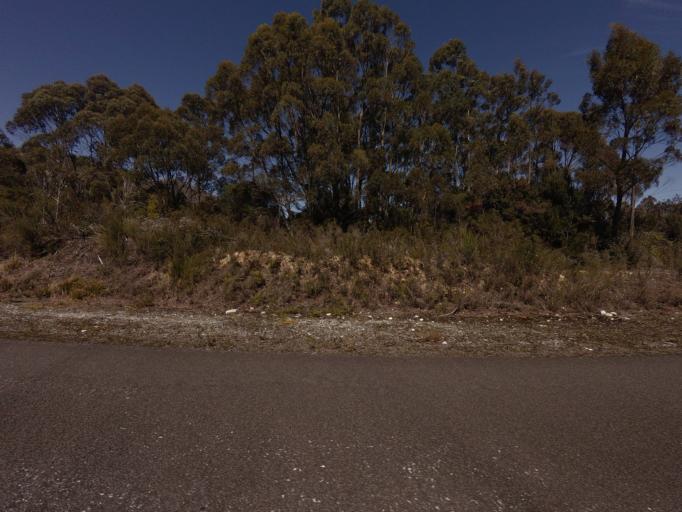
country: AU
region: Tasmania
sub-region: Huon Valley
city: Geeveston
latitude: -42.8337
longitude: 146.1474
